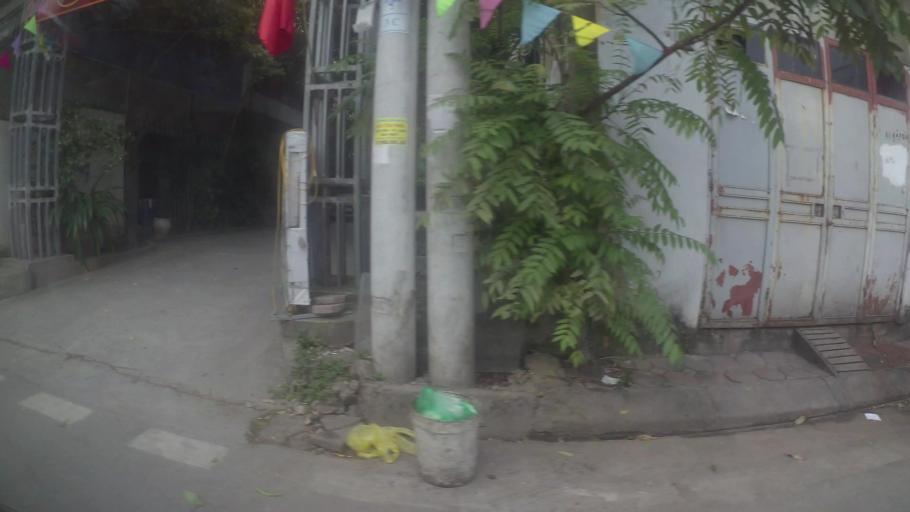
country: VN
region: Ha Noi
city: Cau Dien
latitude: 21.0431
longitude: 105.7525
